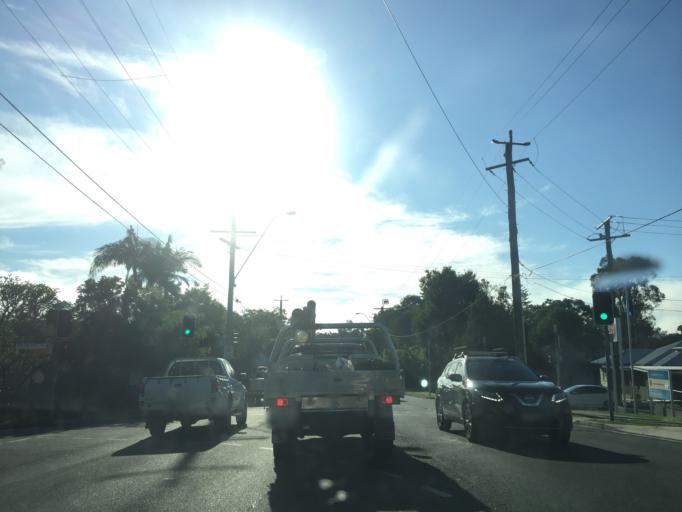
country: AU
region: Queensland
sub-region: Brisbane
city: Toowong
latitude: -27.4488
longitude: 152.9680
